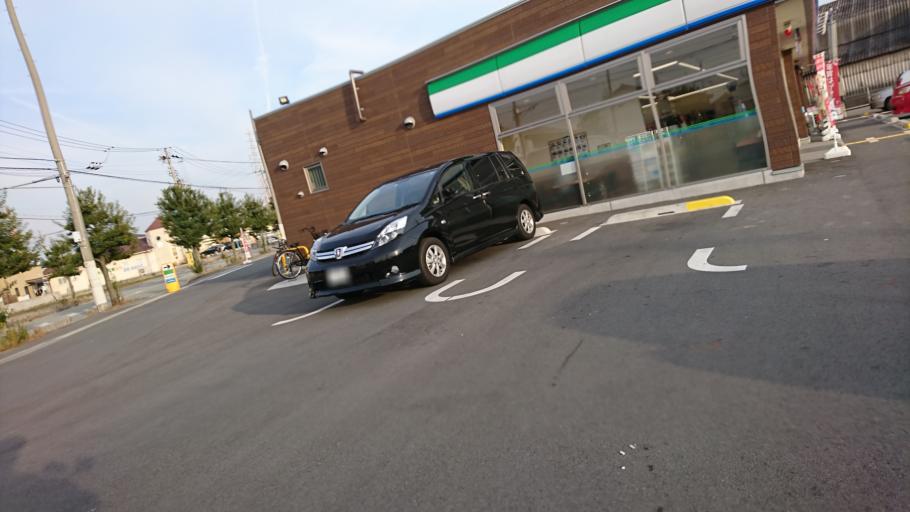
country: JP
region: Hyogo
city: Kakogawacho-honmachi
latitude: 34.7479
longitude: 134.8160
